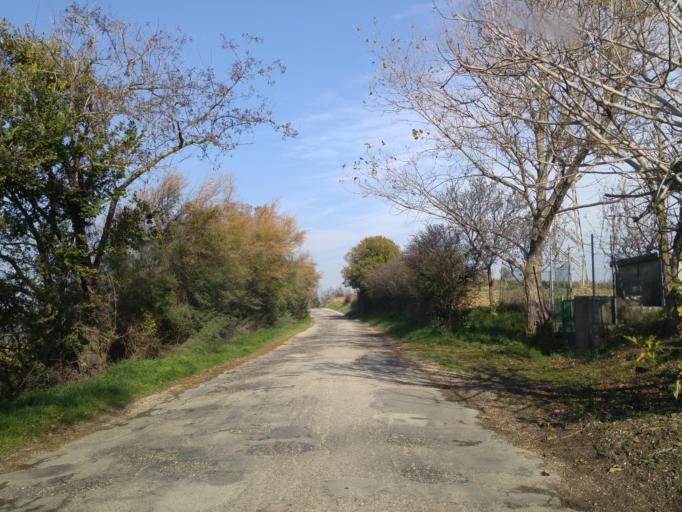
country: IT
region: The Marches
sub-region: Provincia di Pesaro e Urbino
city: Lucrezia
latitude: 43.8053
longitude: 12.9123
